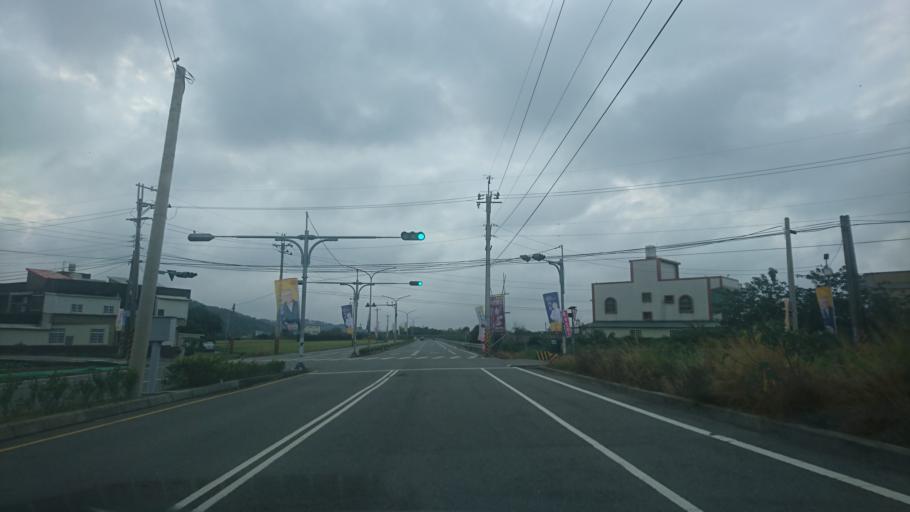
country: TW
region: Taiwan
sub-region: Miaoli
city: Miaoli
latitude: 24.6738
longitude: 120.9064
